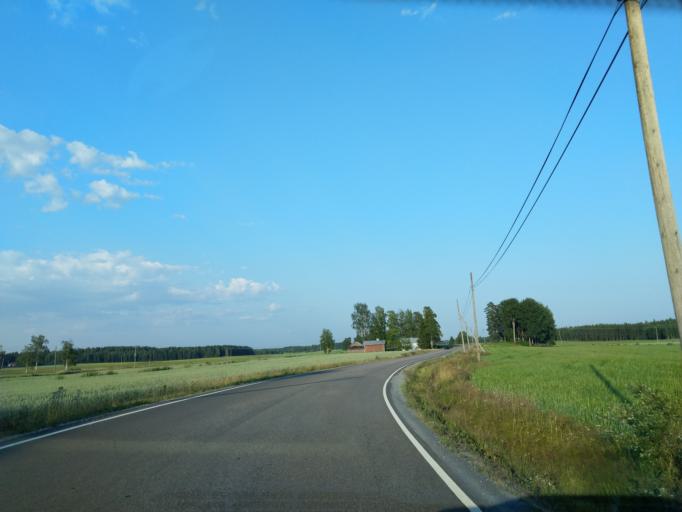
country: FI
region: Satakunta
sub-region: Pohjois-Satakunta
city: Kankaanpaeae
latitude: 61.8202
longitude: 22.3070
